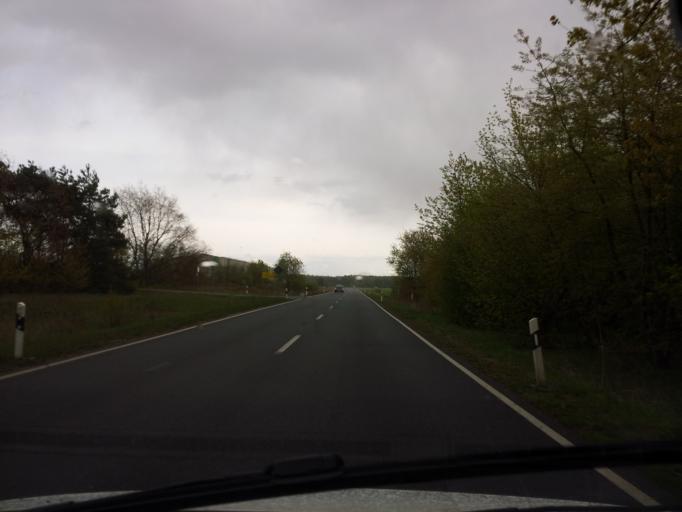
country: DE
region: Brandenburg
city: Heinersbruck
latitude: 51.7847
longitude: 14.4723
